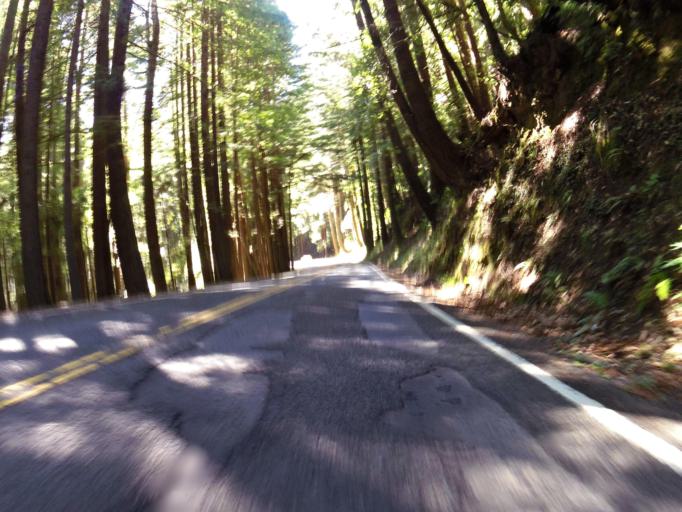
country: US
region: California
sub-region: Humboldt County
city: Redway
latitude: 39.7933
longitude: -123.8167
